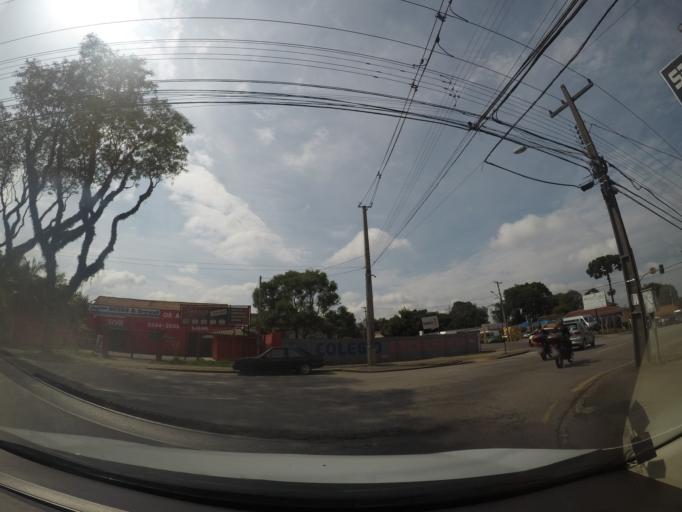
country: BR
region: Parana
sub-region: Curitiba
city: Curitiba
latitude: -25.4922
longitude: -49.2899
